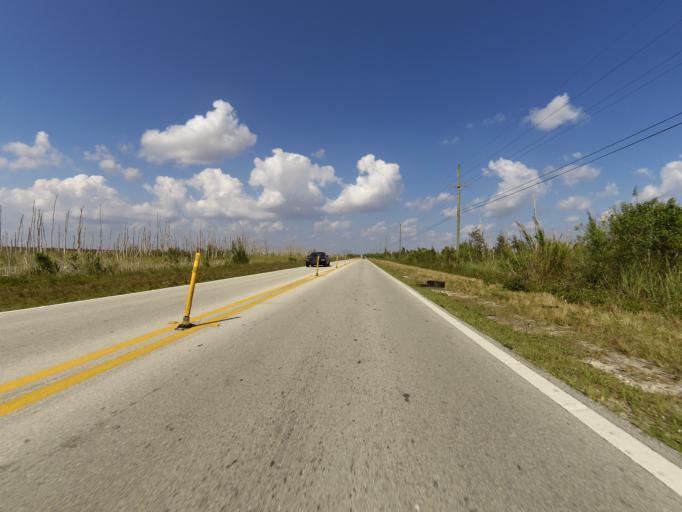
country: US
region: Florida
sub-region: Miami-Dade County
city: Palm Springs North
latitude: 25.9315
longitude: -80.4485
